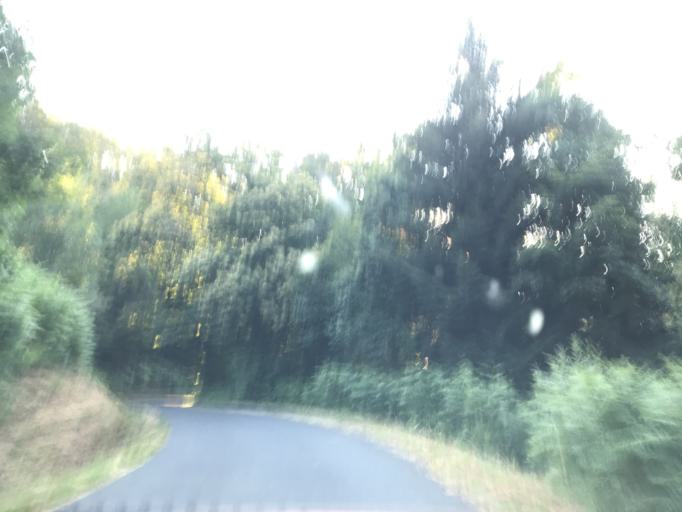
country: FR
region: Auvergne
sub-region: Departement du Puy-de-Dome
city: Courpiere
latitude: 45.7560
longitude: 3.6309
